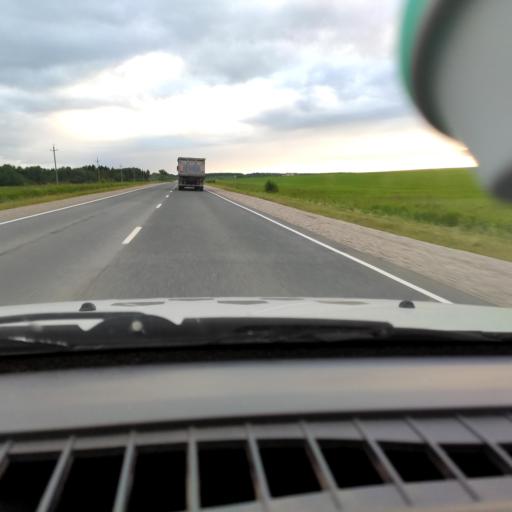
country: RU
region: Perm
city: Kalino
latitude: 58.2870
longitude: 57.4441
